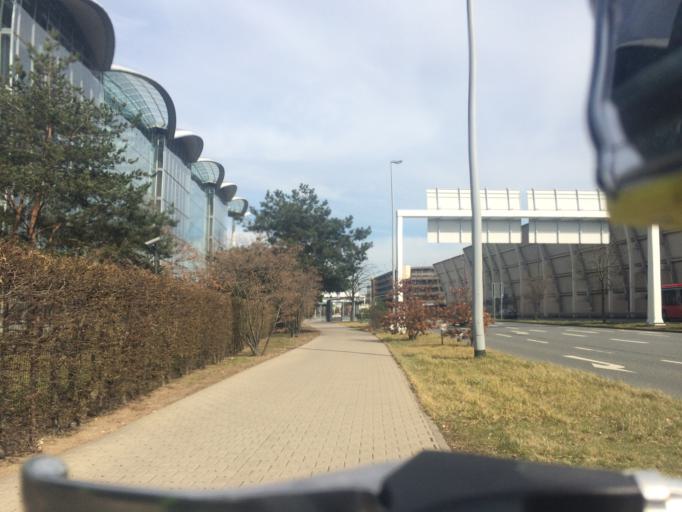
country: DE
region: Hesse
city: Kelsterbach
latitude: 50.0481
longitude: 8.5552
